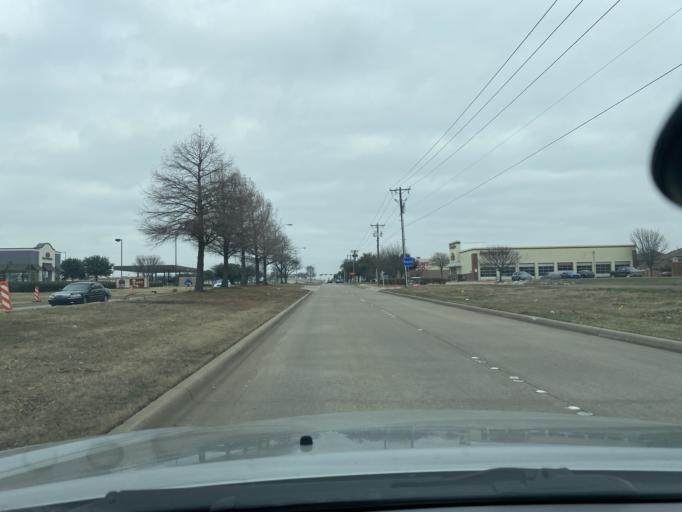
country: US
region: Texas
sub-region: Collin County
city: Frisco
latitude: 33.0951
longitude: -96.7967
